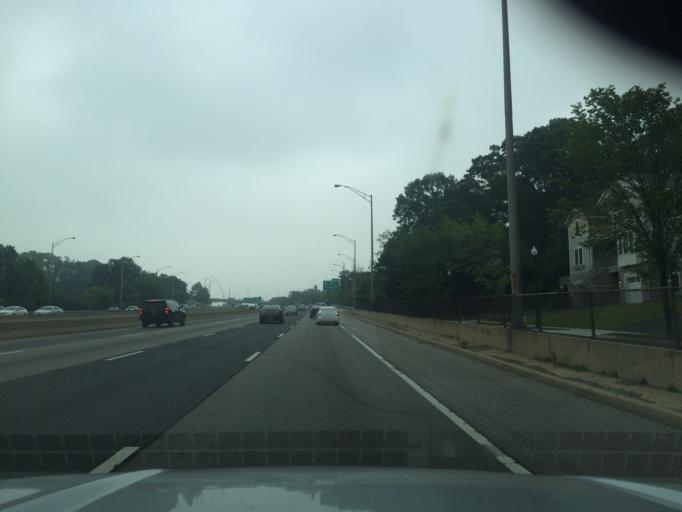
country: US
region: Virginia
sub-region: Arlington County
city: Arlington
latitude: 38.8569
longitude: -77.0714
